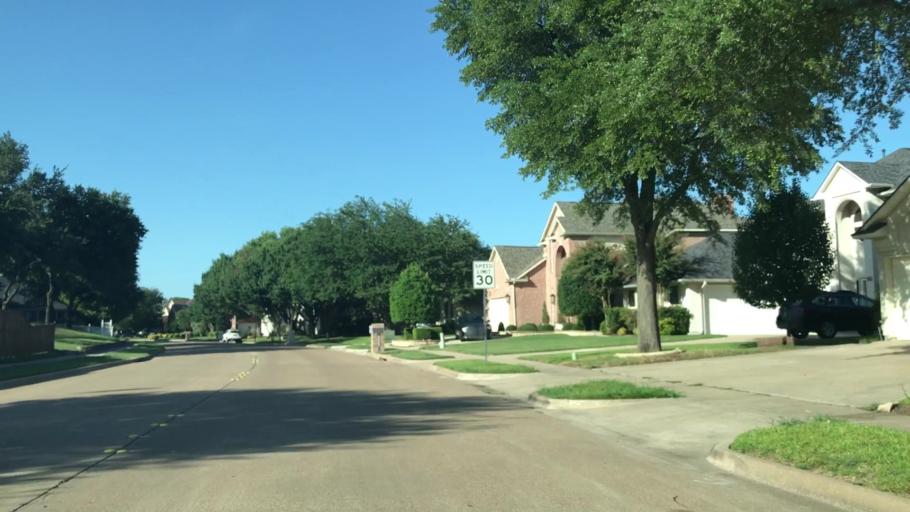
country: US
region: Texas
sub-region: Collin County
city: Frisco
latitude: 33.1209
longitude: -96.7789
